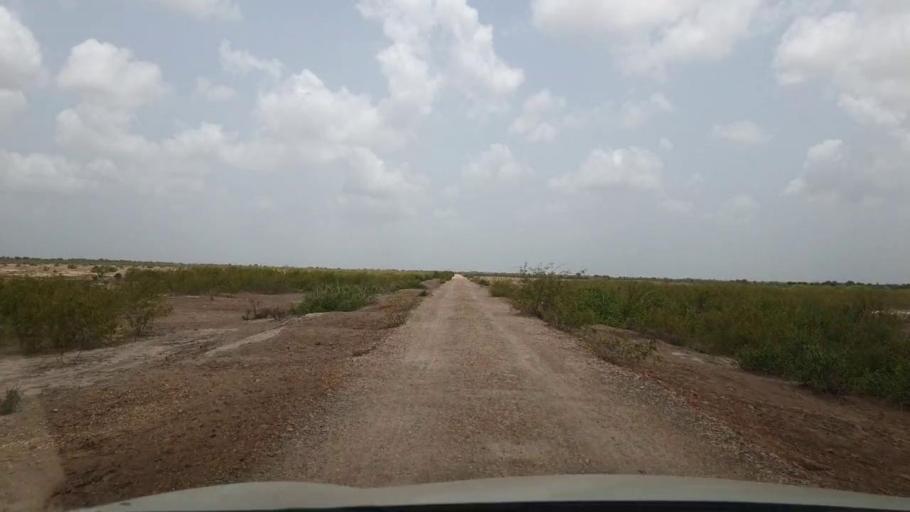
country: PK
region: Sindh
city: Chambar
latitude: 25.2240
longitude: 68.7596
